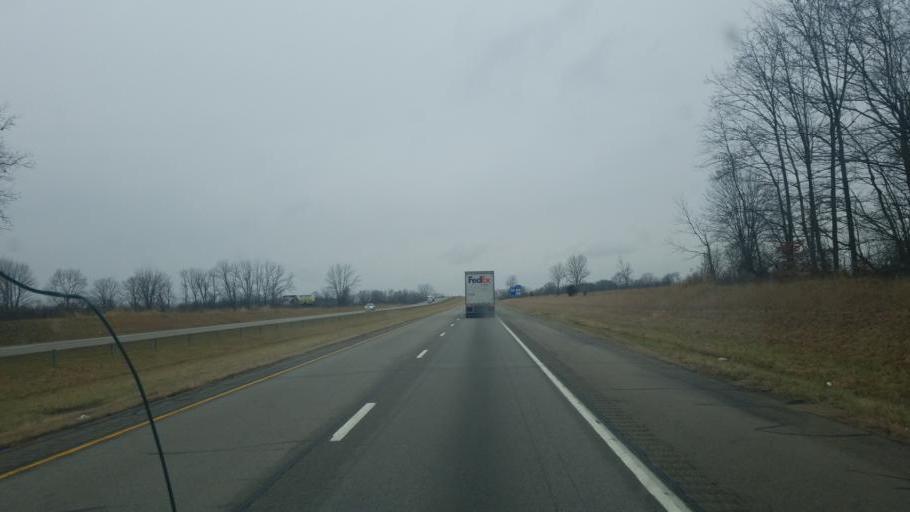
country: US
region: Indiana
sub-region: Wayne County
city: Cambridge City
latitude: 39.8532
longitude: -85.2363
